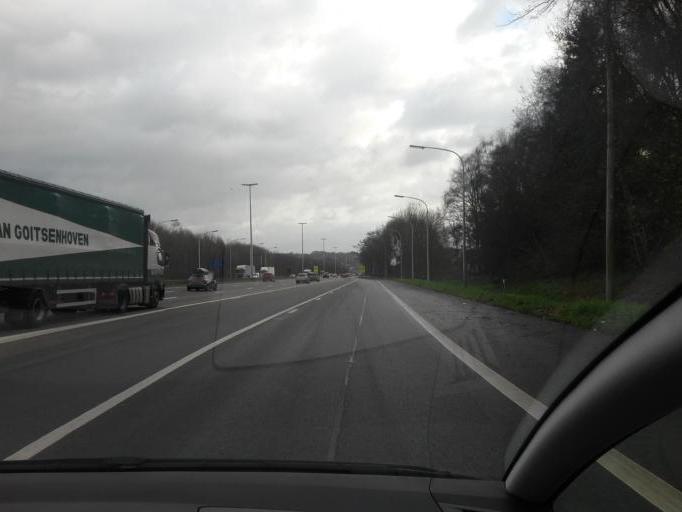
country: BE
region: Wallonia
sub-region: Province du Brabant Wallon
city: Wavre
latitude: 50.7173
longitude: 4.5865
